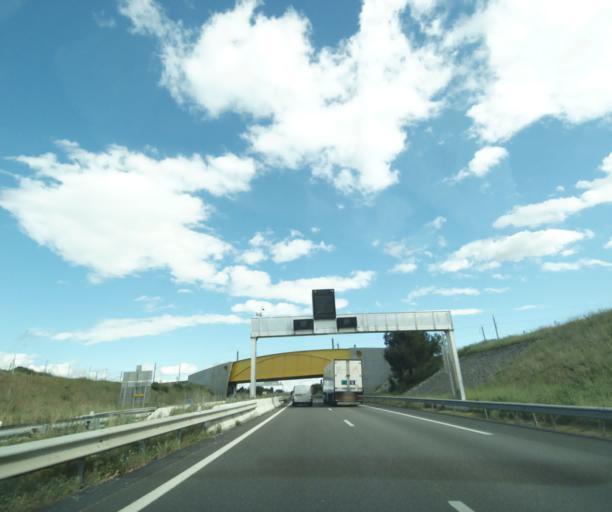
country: FR
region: Languedoc-Roussillon
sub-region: Departement du Gard
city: Bouillargues
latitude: 43.7841
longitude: 4.4058
